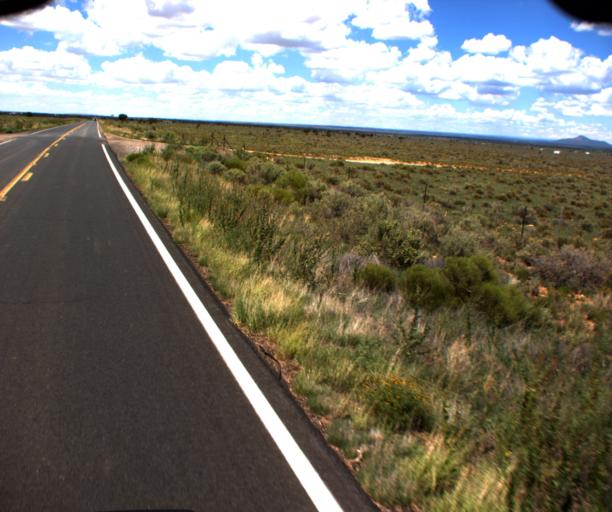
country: US
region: Arizona
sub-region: Coconino County
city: Williams
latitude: 35.6264
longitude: -112.1135
